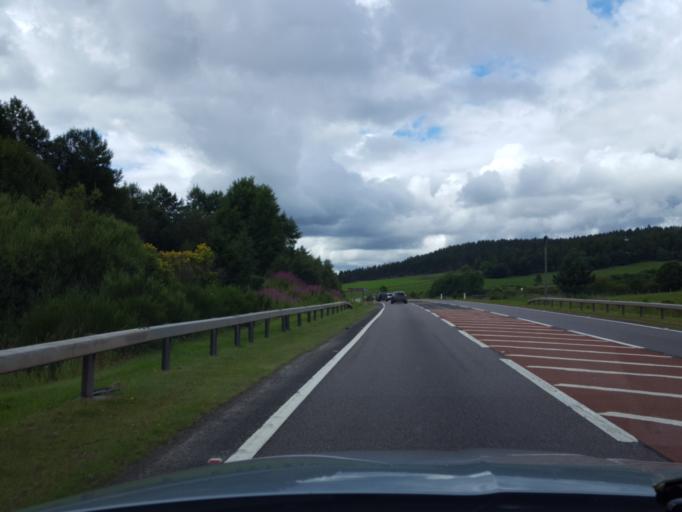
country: GB
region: Scotland
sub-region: Highland
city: Grantown on Spey
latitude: 57.3158
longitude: -3.6249
